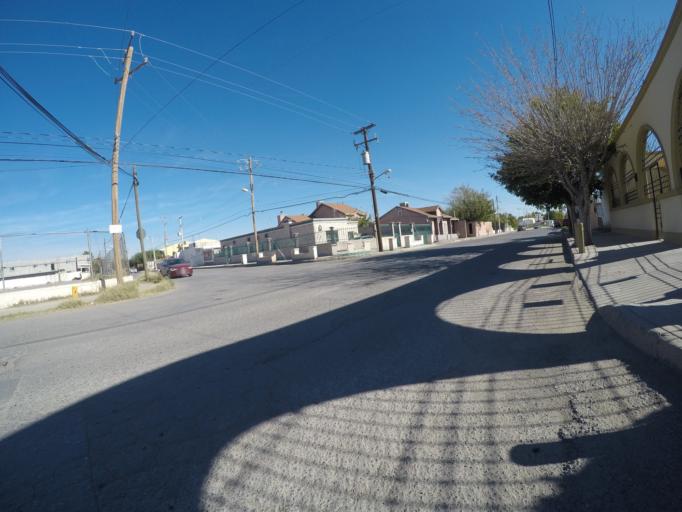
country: MX
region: Chihuahua
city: Ciudad Juarez
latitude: 31.7397
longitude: -106.4368
